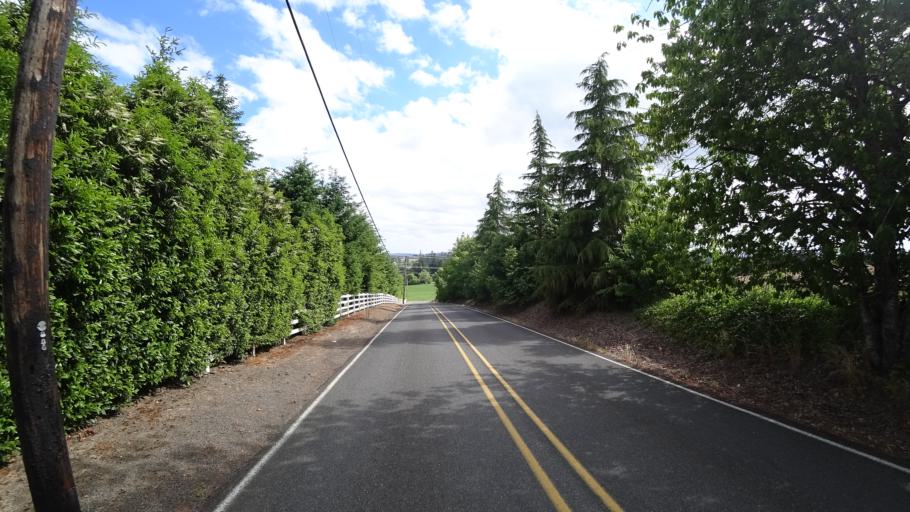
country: US
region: Oregon
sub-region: Washington County
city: Bethany
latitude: 45.5860
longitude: -122.8418
